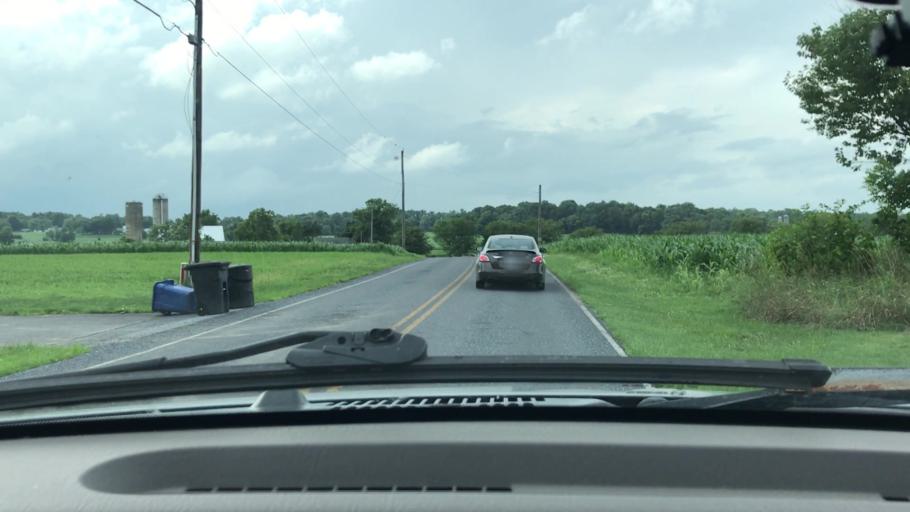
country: US
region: Pennsylvania
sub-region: Lancaster County
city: Elizabethtown
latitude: 40.1675
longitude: -76.5825
